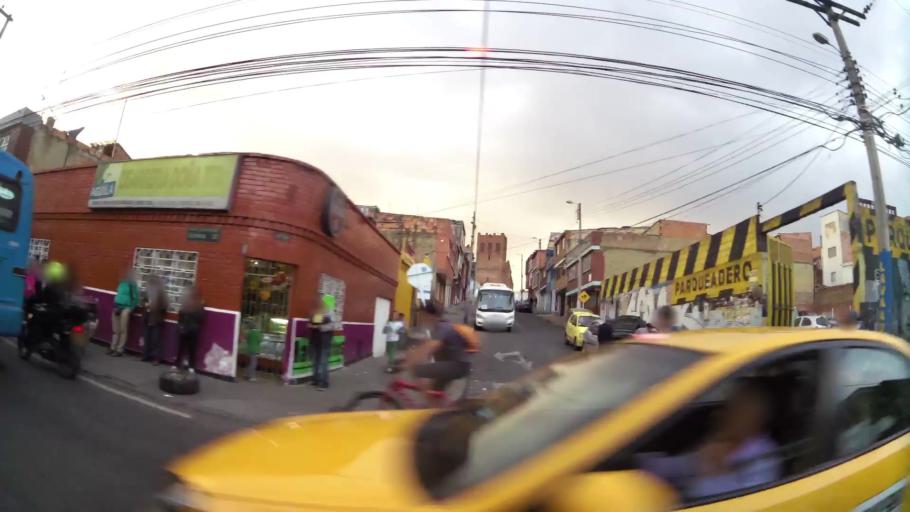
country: CO
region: Bogota D.C.
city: Bogota
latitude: 4.5842
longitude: -74.1380
